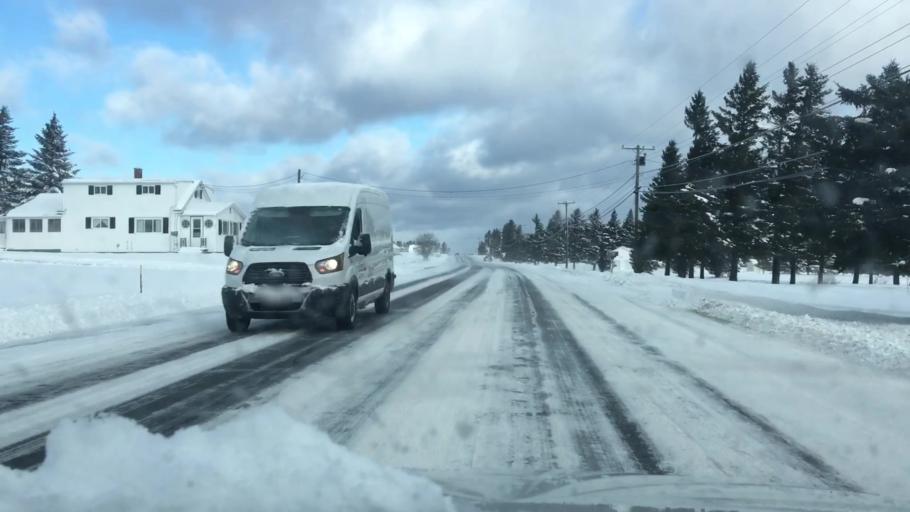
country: US
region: Maine
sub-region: Aroostook County
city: Caribou
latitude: 46.9060
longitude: -68.0159
